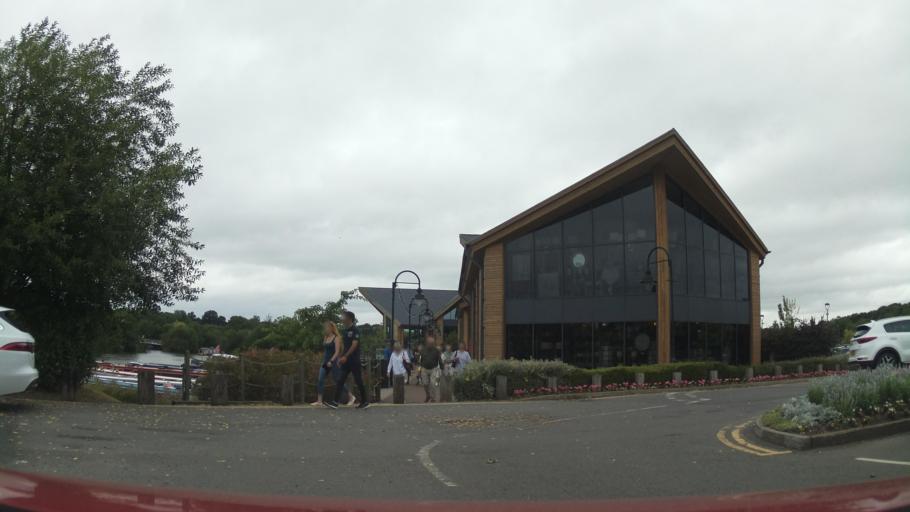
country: GB
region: England
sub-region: Derbyshire
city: Findern
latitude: 52.8606
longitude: -1.5534
